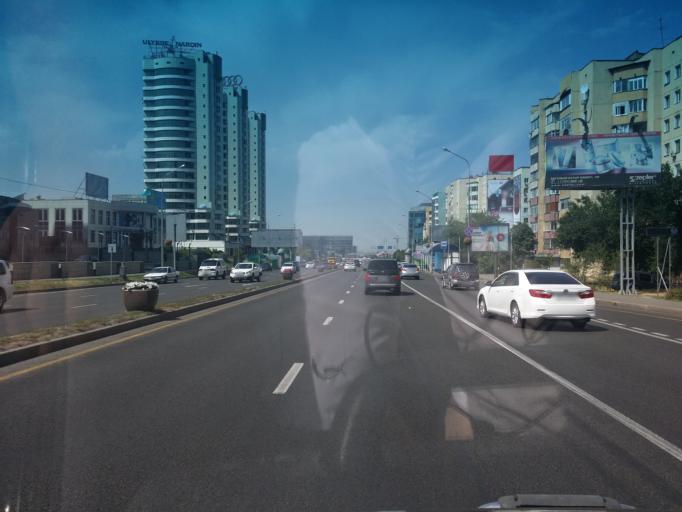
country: KZ
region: Almaty Qalasy
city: Almaty
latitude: 43.2285
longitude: 76.9559
